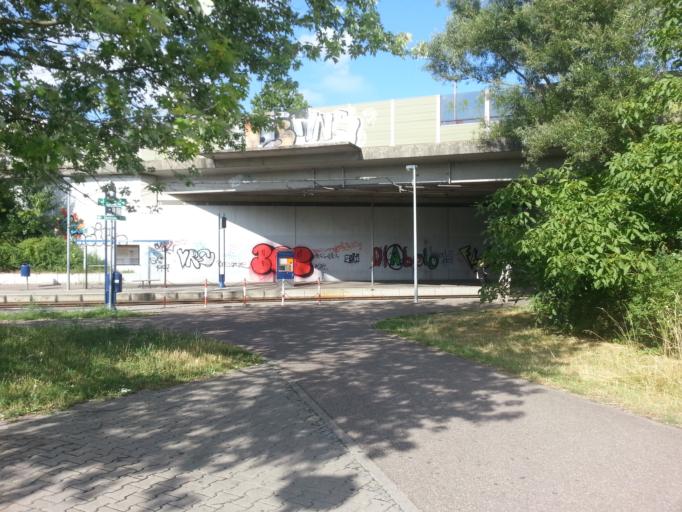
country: DE
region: Baden-Wuerttemberg
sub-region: Karlsruhe Region
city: Ilvesheim
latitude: 49.5063
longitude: 8.5312
